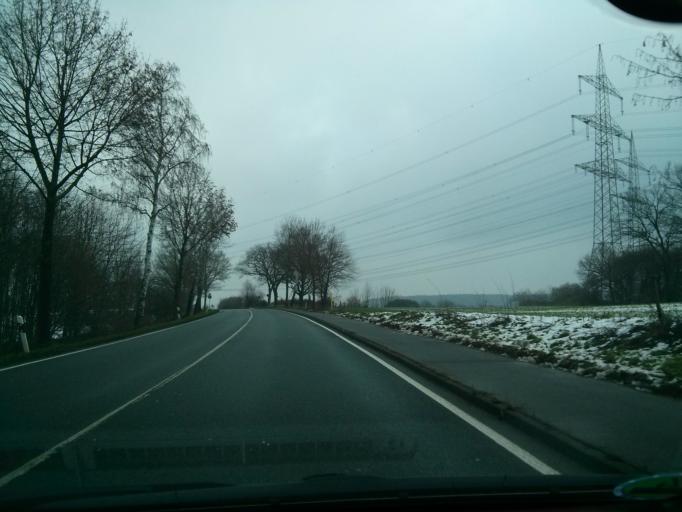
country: DE
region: North Rhine-Westphalia
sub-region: Regierungsbezirk Koln
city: Alfter
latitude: 50.6952
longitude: 7.0073
